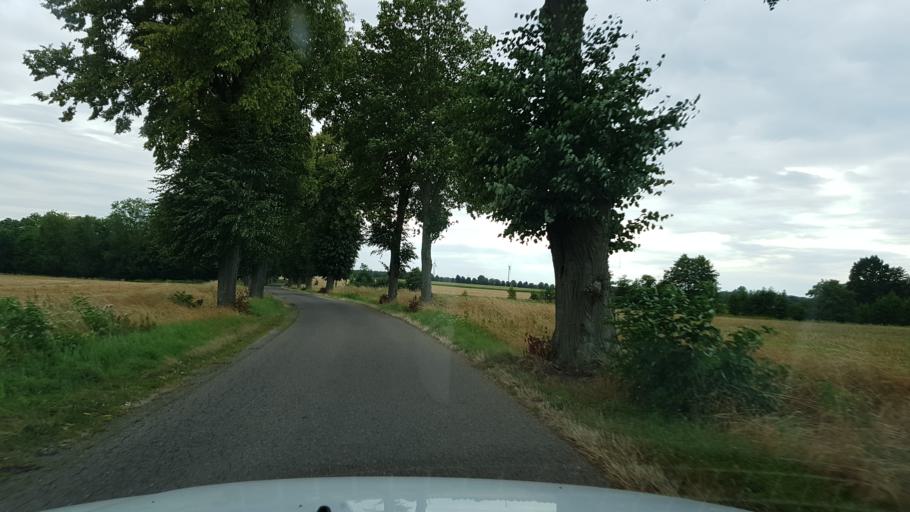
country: PL
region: West Pomeranian Voivodeship
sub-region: Powiat bialogardzki
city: Karlino
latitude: 54.1160
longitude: 15.8677
